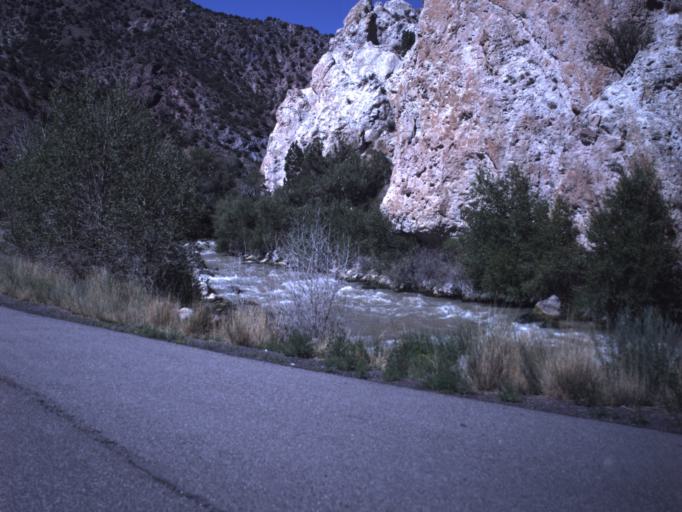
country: US
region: Utah
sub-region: Sevier County
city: Monroe
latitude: 38.5686
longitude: -112.2529
